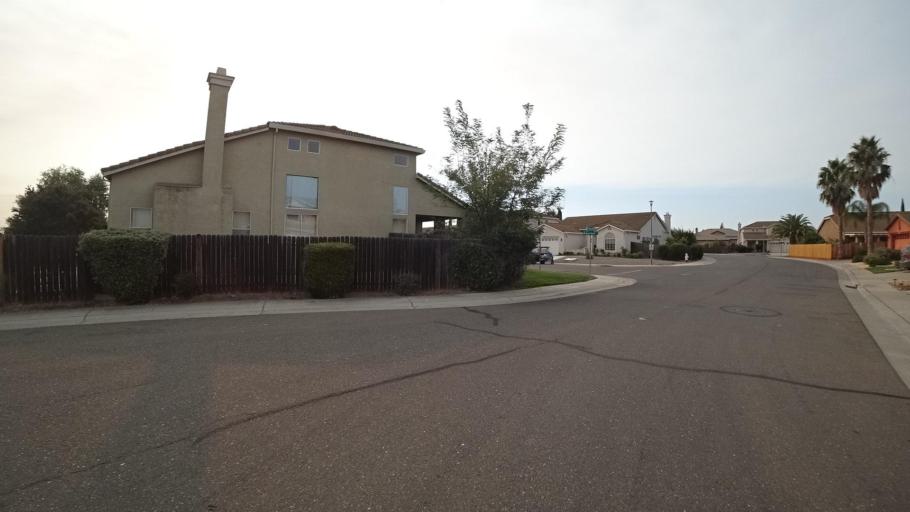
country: US
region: California
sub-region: Sacramento County
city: Laguna
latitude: 38.4300
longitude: -121.4044
